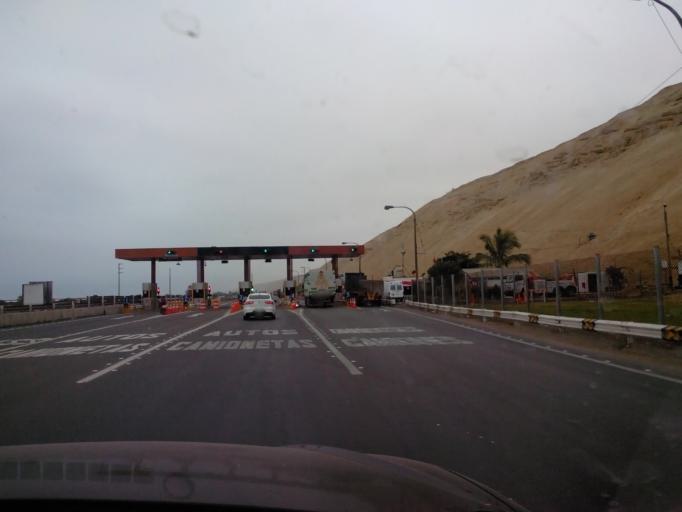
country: PE
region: Ica
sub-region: Provincia de Chincha
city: San Pedro
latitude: -13.3875
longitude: -76.2017
